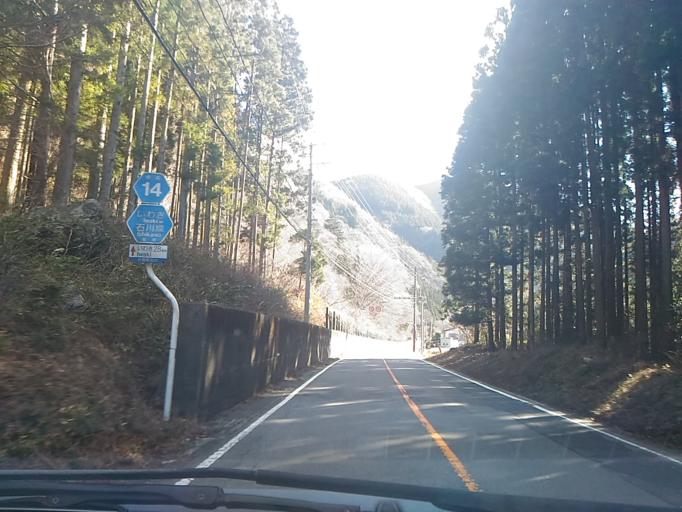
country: JP
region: Fukushima
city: Ishikawa
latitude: 37.0531
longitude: 140.6127
